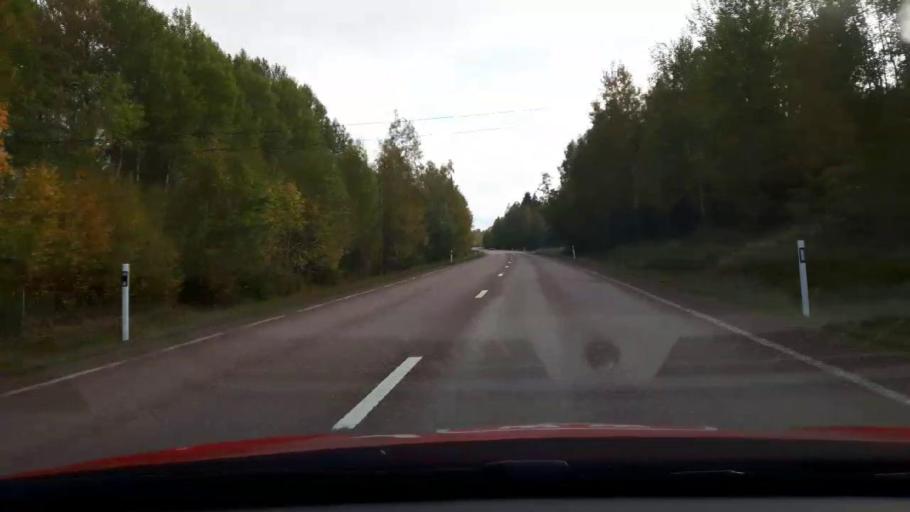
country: SE
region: Gaevleborg
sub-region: Ljusdals Kommun
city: Jaervsoe
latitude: 61.6460
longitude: 16.2058
